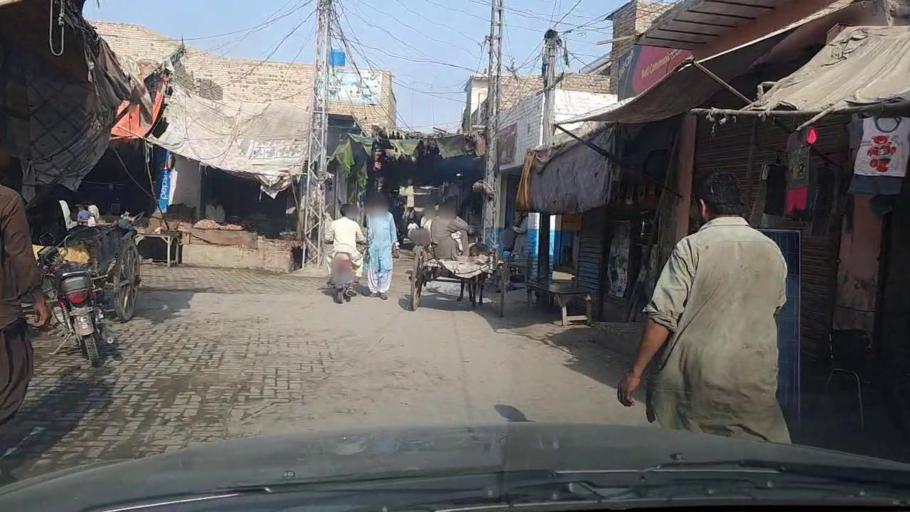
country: PK
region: Sindh
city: Pir jo Goth
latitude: 27.5573
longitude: 68.5525
